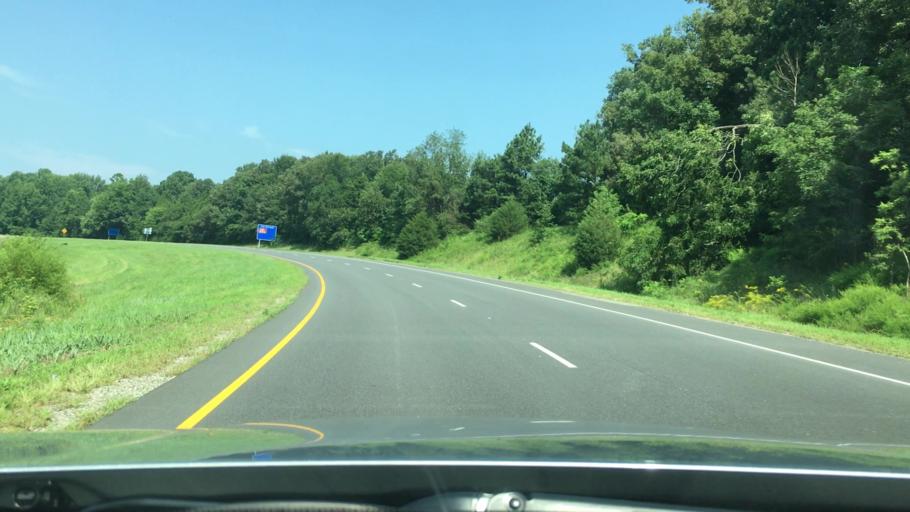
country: US
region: Virginia
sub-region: Caroline County
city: Bowling Green
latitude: 38.0390
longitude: -77.3566
